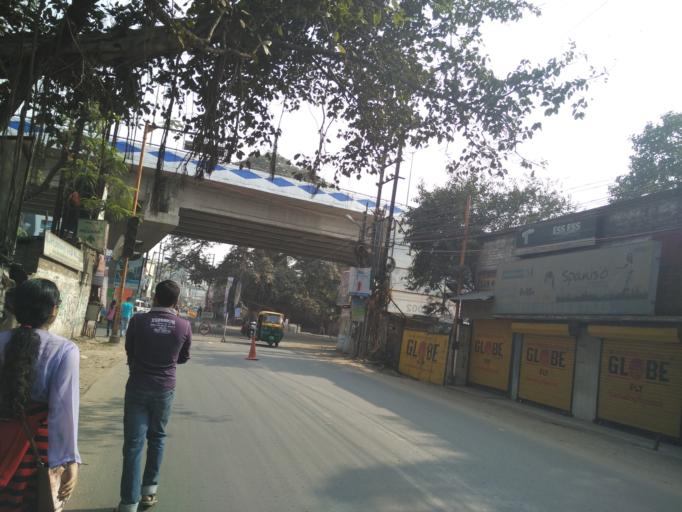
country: IN
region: West Bengal
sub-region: South 24 Paraganas
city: Baruipur
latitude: 22.4498
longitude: 88.3906
